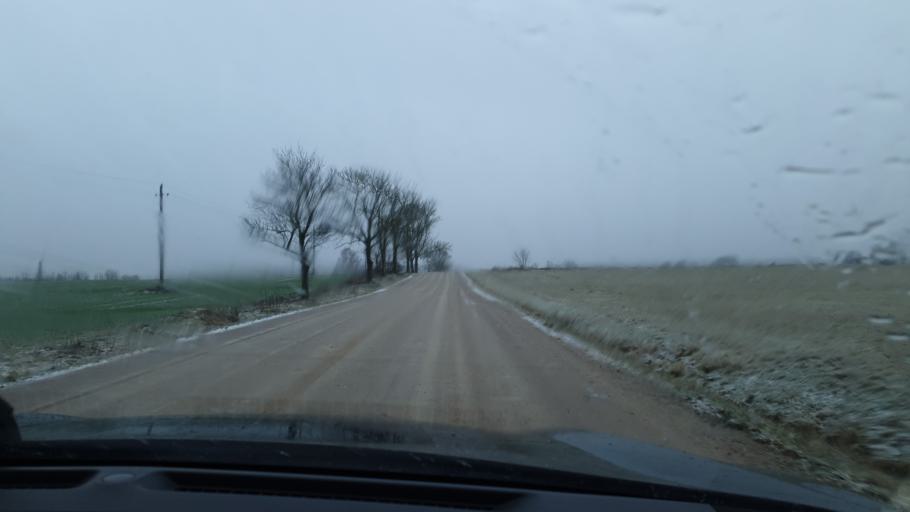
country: LT
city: Jieznas
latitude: 54.5808
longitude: 24.3166
